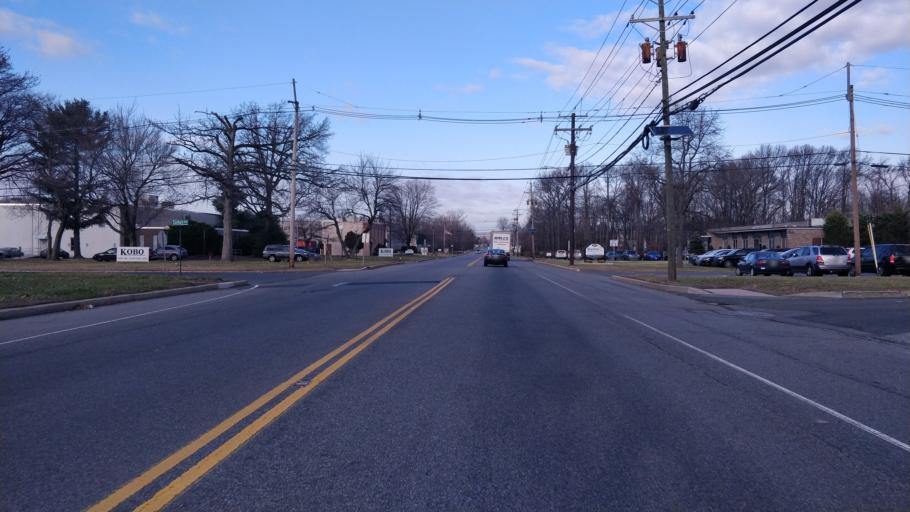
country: US
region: New Jersey
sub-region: Middlesex County
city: South Plainfield
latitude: 40.5688
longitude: -74.4300
